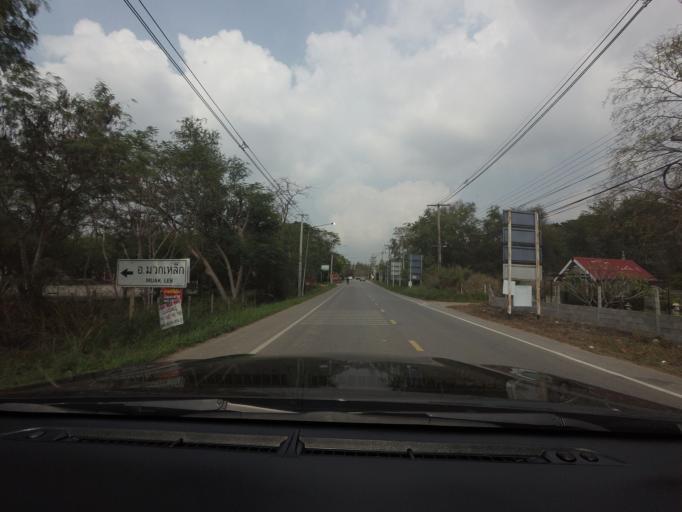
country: TH
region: Sara Buri
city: Muak Lek
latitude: 14.6322
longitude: 101.2123
